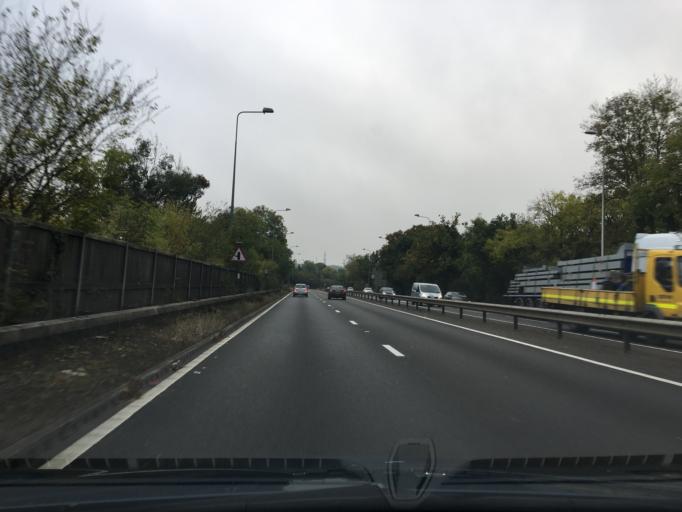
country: GB
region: England
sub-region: Surrey
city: Guildford
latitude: 51.2384
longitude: -0.6009
